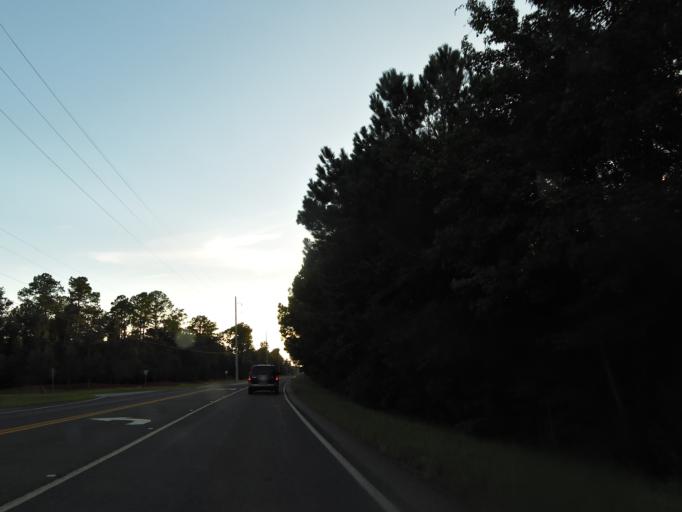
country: US
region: Georgia
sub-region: Glynn County
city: Brunswick
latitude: 31.1095
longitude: -81.6191
